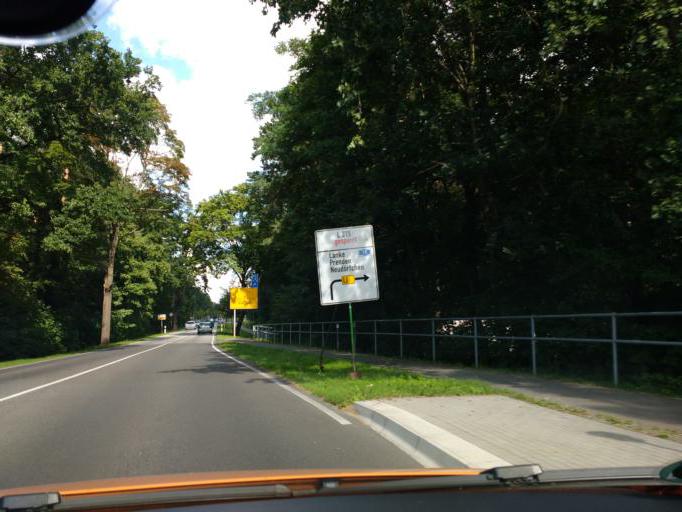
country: DE
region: Brandenburg
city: Wandlitz
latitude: 52.7660
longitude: 13.4751
